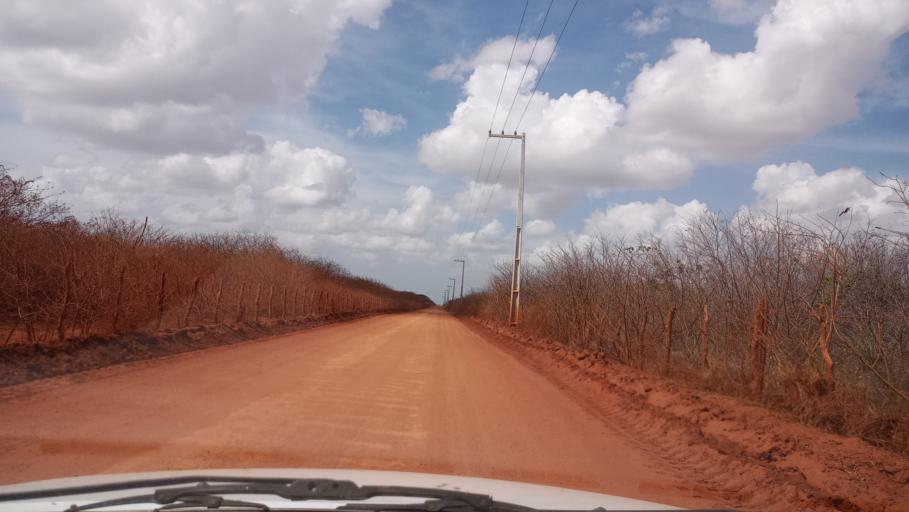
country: BR
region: Rio Grande do Norte
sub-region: Joao Camara
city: Joao Camara
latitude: -5.3606
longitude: -35.8347
